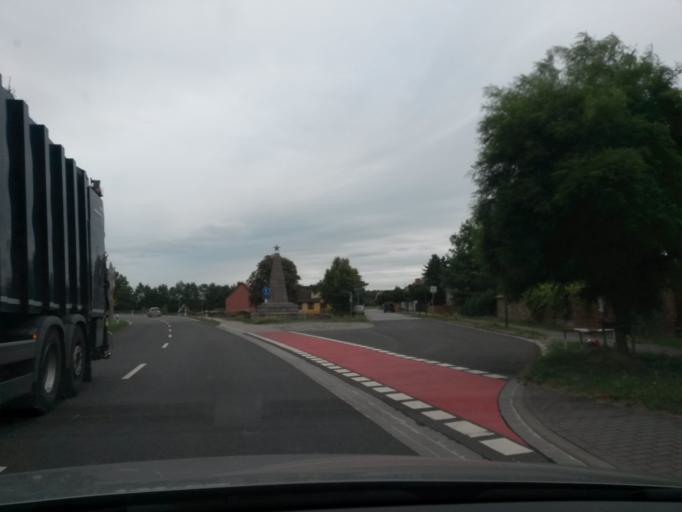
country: DE
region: Saxony-Anhalt
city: Klietz
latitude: 52.6977
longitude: 12.0719
